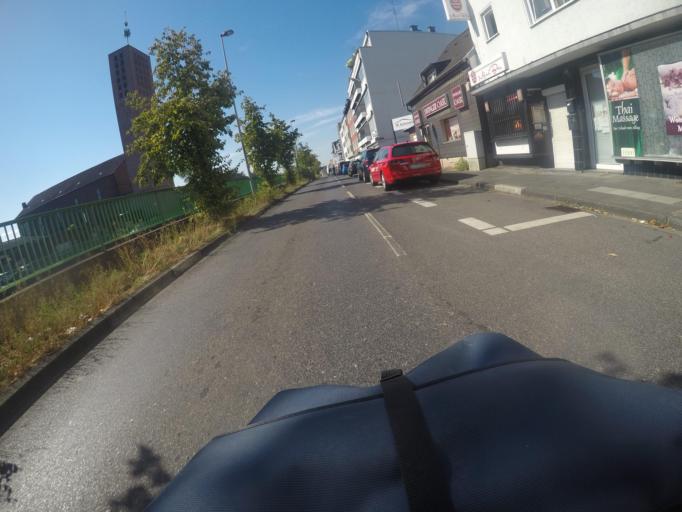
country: DE
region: North Rhine-Westphalia
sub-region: Regierungsbezirk Koln
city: Leverkusen
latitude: 51.0482
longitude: 6.9954
